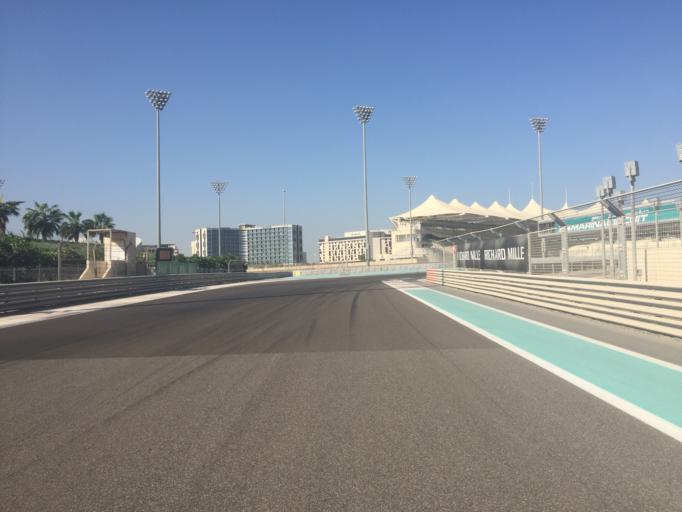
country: AE
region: Abu Dhabi
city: Abu Dhabi
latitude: 24.4678
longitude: 54.6042
